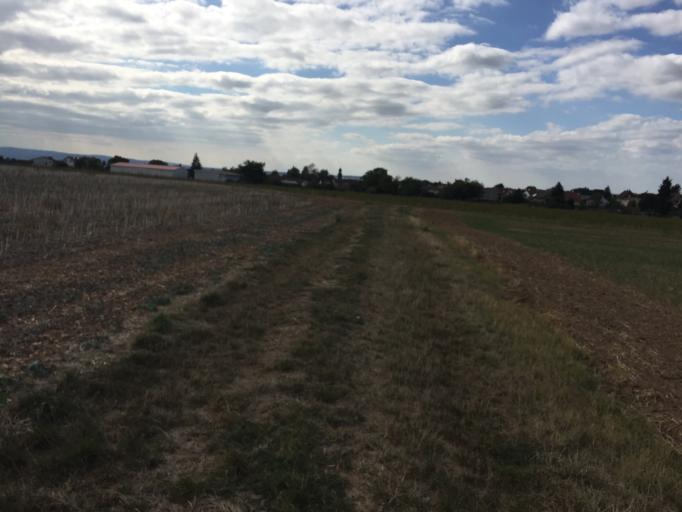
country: DE
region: Hesse
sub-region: Regierungsbezirk Giessen
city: Lich
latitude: 50.4949
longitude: 8.8224
